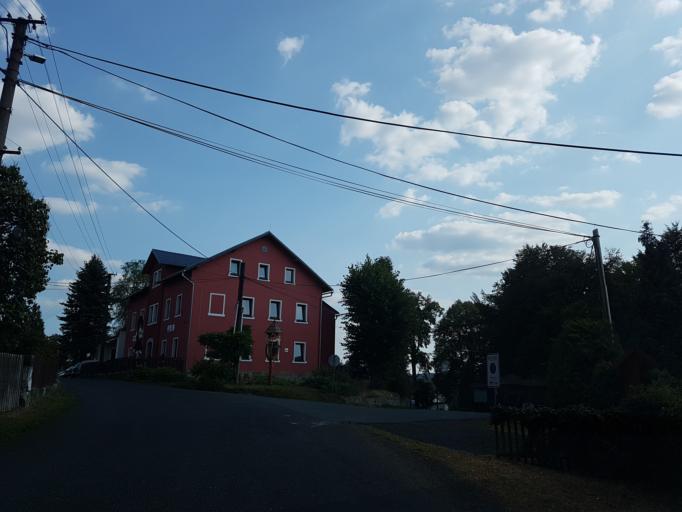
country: CZ
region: Ustecky
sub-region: Okres Decin
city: Decin
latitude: 50.8599
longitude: 14.2658
